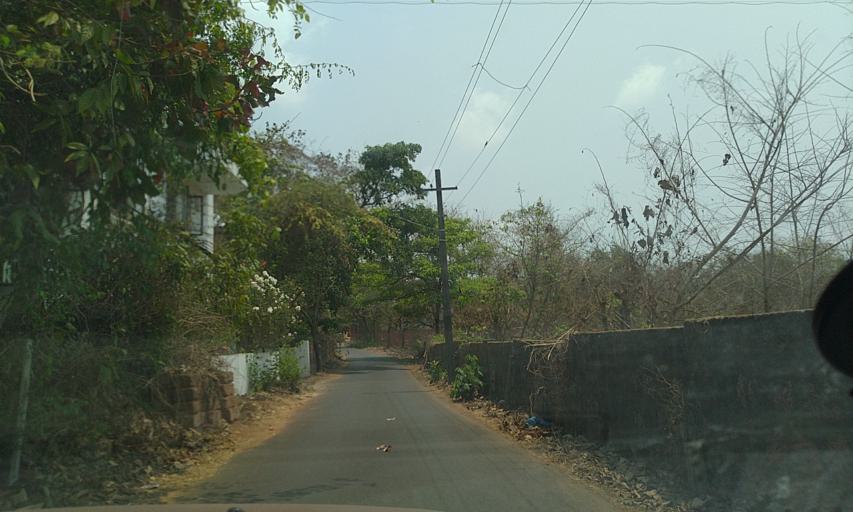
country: IN
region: Goa
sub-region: North Goa
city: Panaji
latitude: 15.5220
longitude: 73.8237
